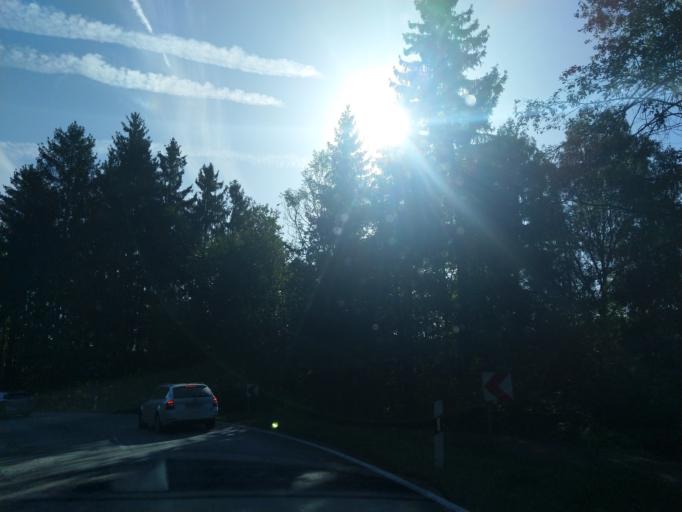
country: DE
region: Bavaria
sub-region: Lower Bavaria
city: Bernried
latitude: 48.9236
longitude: 12.9217
